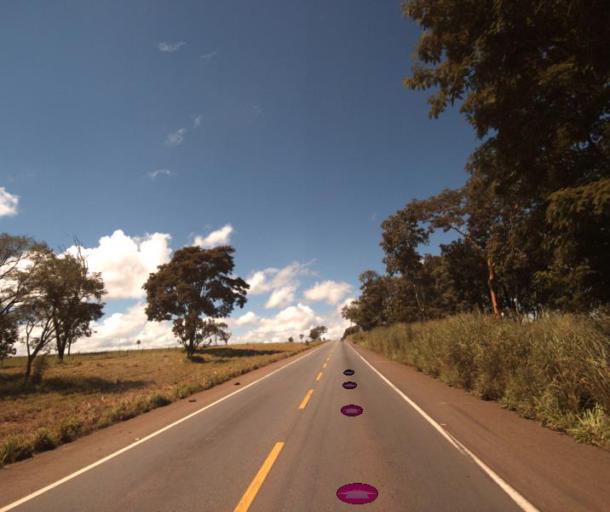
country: BR
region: Goias
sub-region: Jaragua
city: Jaragua
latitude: -15.8235
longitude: -49.2843
